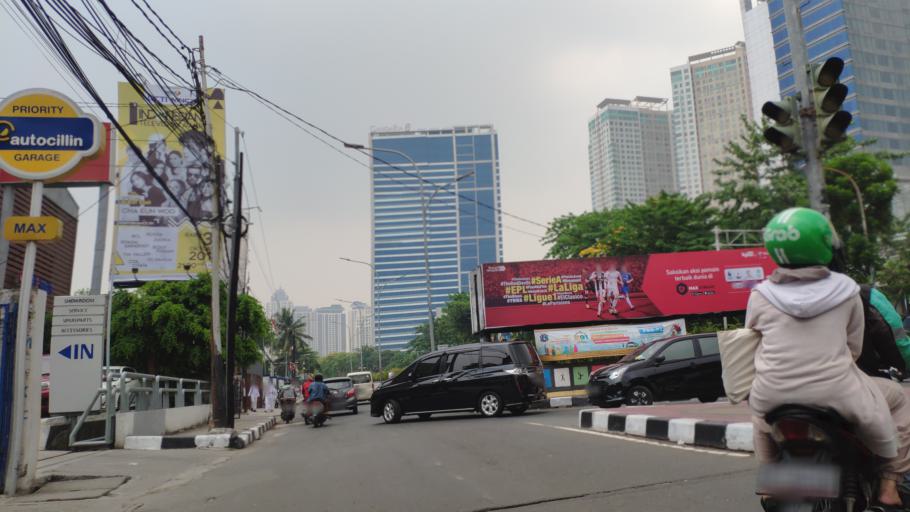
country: ID
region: Jakarta Raya
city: Jakarta
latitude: -6.2459
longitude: 106.7817
